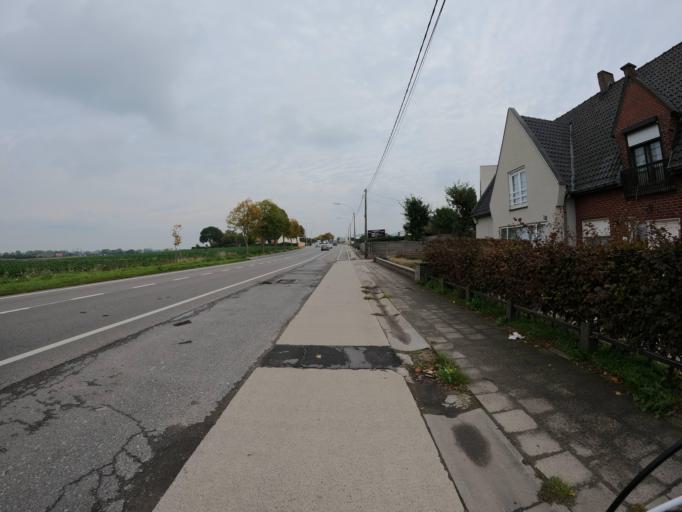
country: BE
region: Flanders
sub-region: Provincie West-Vlaanderen
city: Tielt
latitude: 51.0048
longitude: 3.3410
